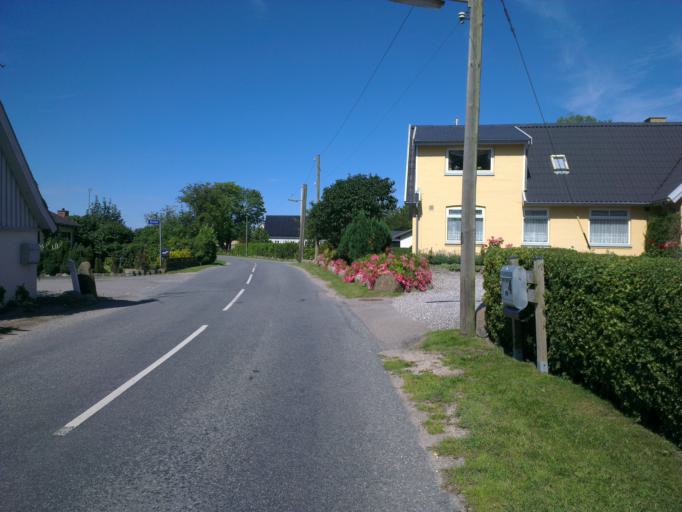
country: DK
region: Capital Region
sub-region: Frederikssund Kommune
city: Frederikssund
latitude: 55.8616
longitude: 12.0967
